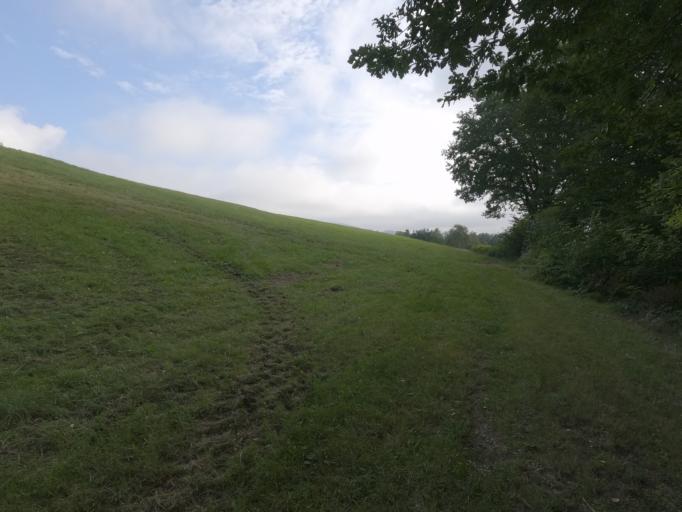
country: DE
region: Bavaria
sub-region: Lower Bavaria
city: Niederalteich
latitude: 48.8053
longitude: 13.0282
